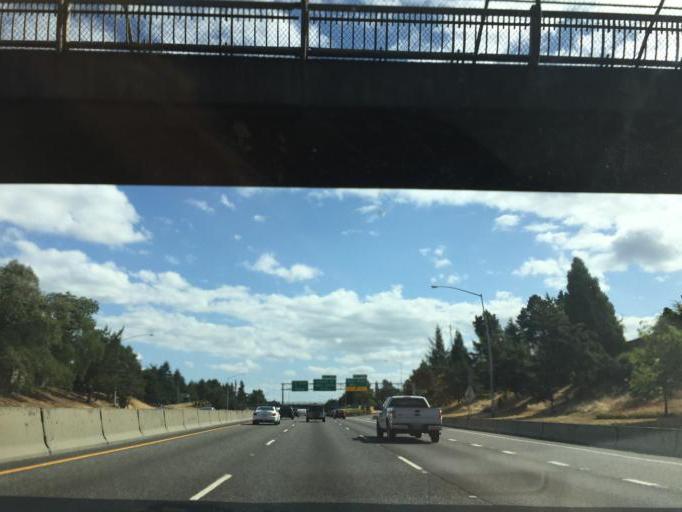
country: US
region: Oregon
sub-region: Multnomah County
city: Portland
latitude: 45.5733
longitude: -122.6788
